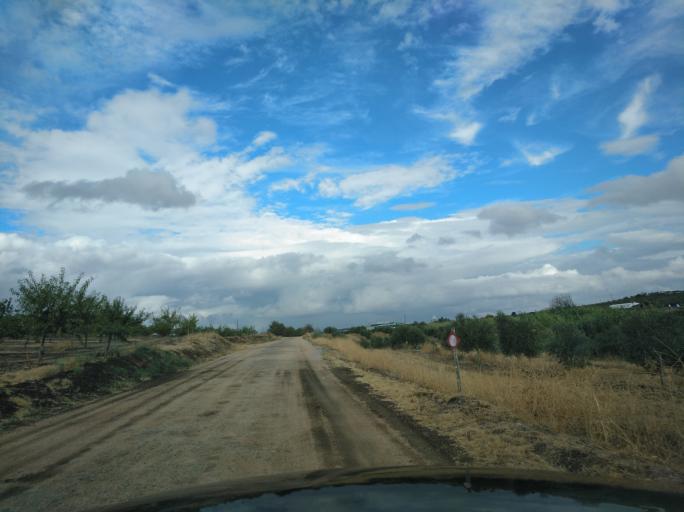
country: PT
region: Portalegre
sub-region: Campo Maior
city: Campo Maior
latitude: 39.0393
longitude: -7.1124
